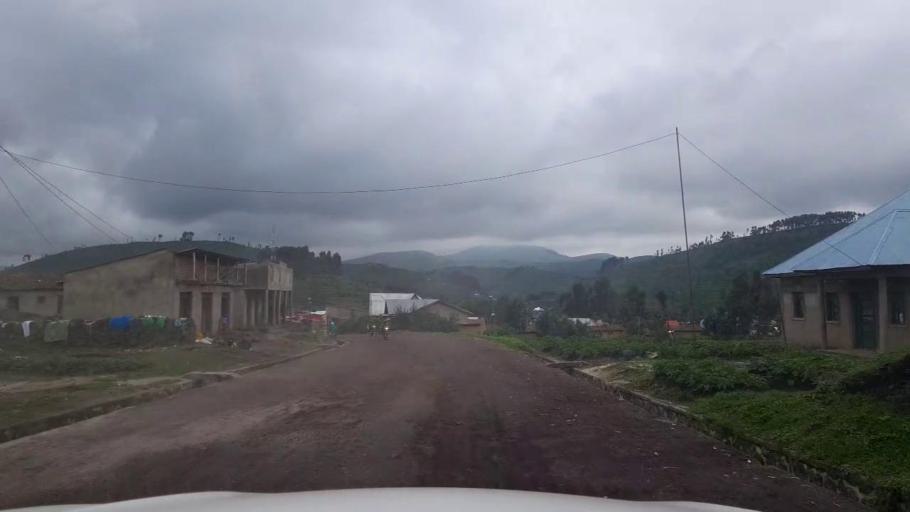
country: RW
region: Northern Province
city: Musanze
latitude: -1.6083
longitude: 29.4519
